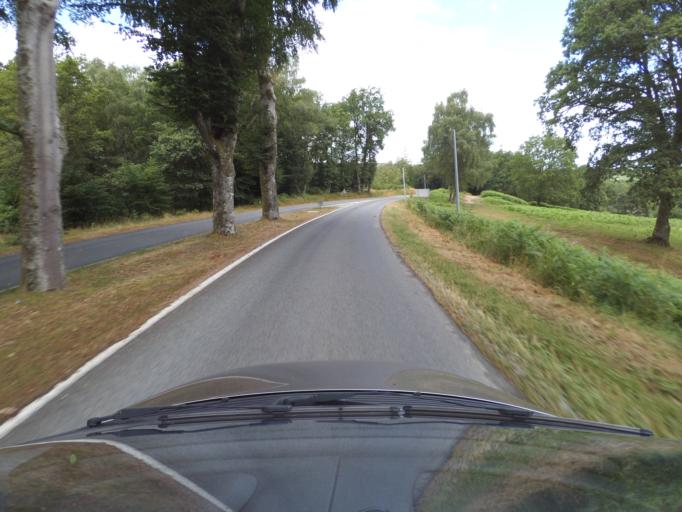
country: FR
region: Limousin
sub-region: Departement de la Haute-Vienne
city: Peyrat-le-Chateau
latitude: 45.8455
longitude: 1.9060
